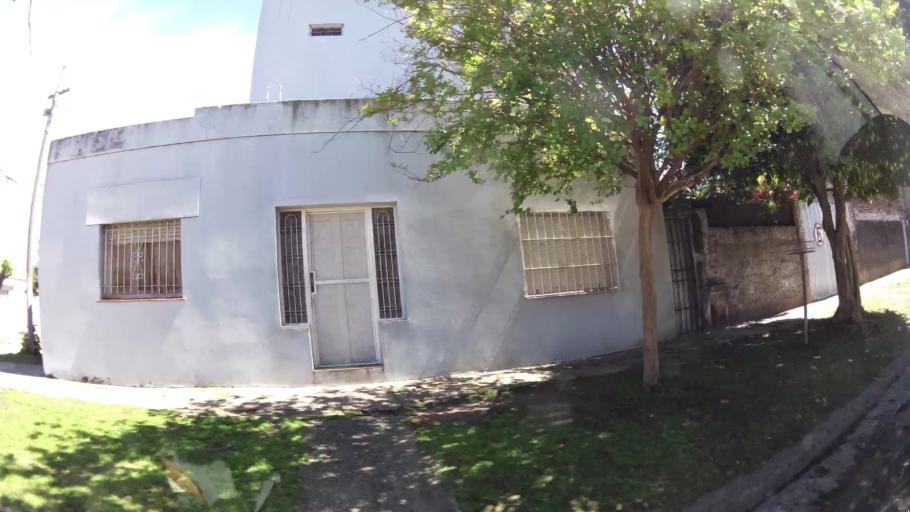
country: AR
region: Buenos Aires
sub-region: Partido de Quilmes
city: Quilmes
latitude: -34.7087
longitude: -58.2657
